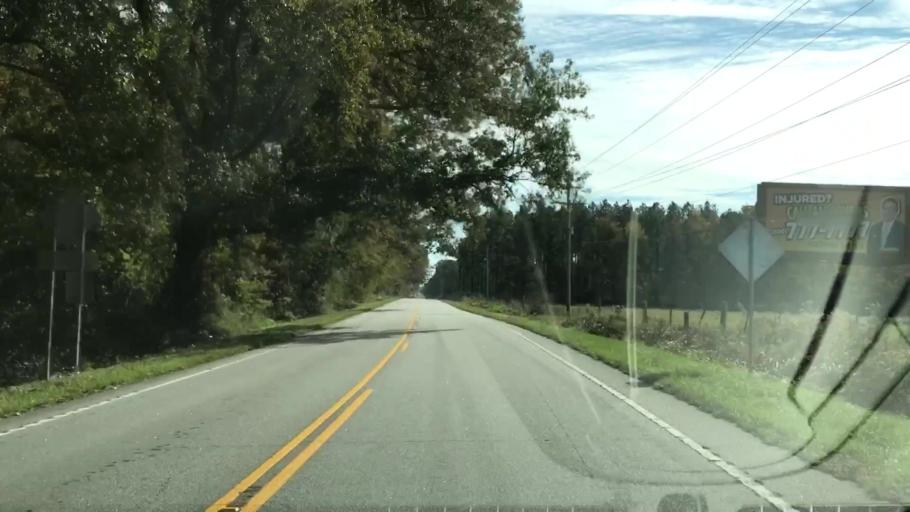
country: US
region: South Carolina
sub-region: Colleton County
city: Walterboro
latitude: 32.8228
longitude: -80.5559
